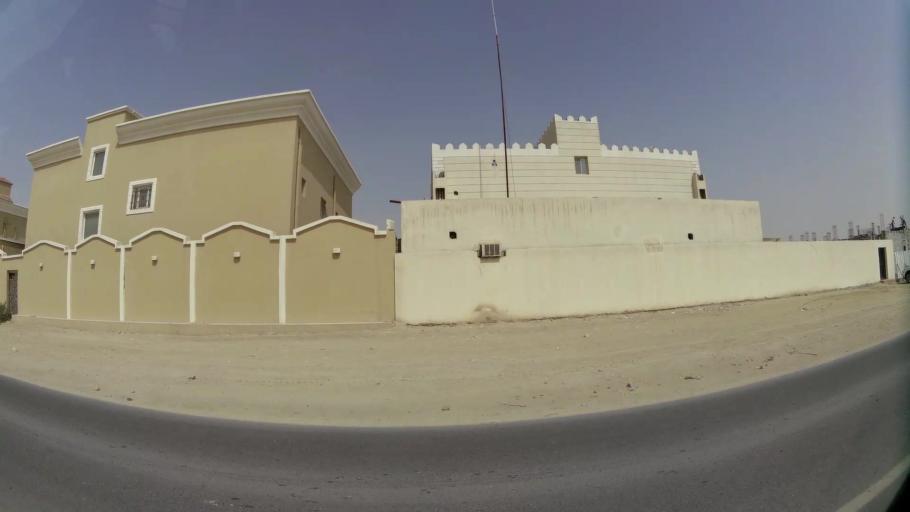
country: QA
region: Baladiyat ar Rayyan
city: Ar Rayyan
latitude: 25.2404
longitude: 51.3651
